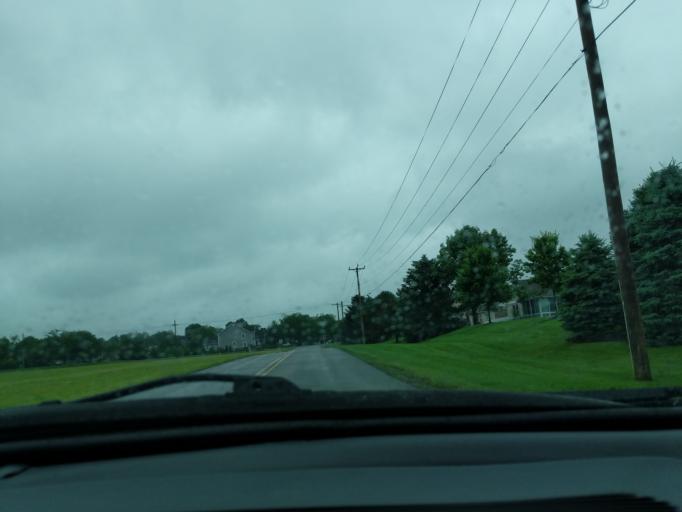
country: US
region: Indiana
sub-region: Hamilton County
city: Cicero
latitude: 40.1018
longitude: -86.0311
